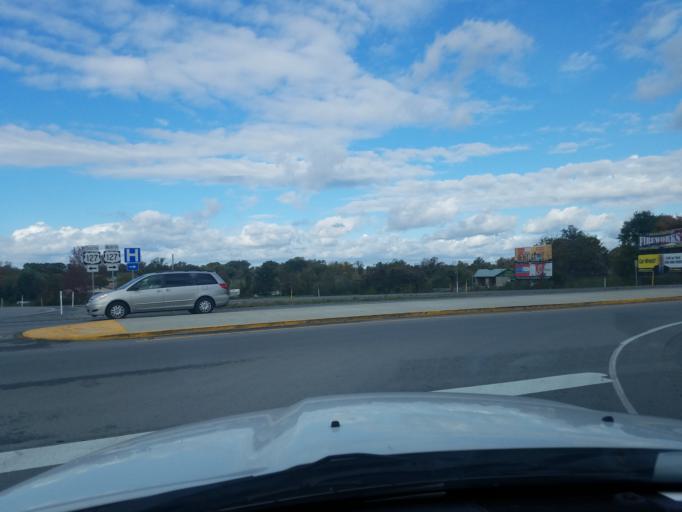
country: US
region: Kentucky
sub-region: Russell County
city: Russell Springs
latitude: 37.0531
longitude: -85.0700
